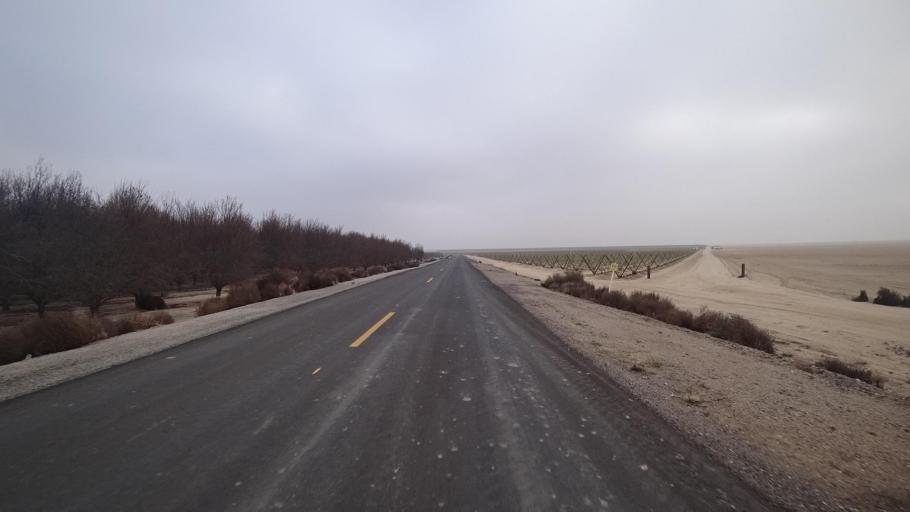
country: US
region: California
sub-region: Kern County
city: Maricopa
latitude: 35.1205
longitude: -119.3588
